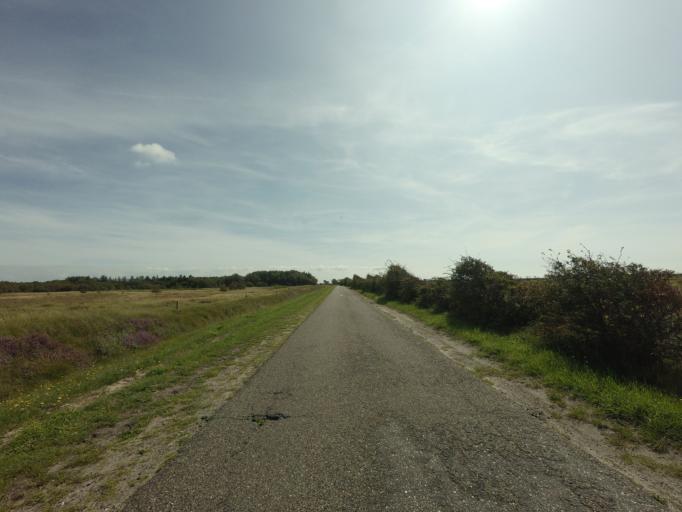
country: NL
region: Friesland
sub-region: Gemeente Ameland
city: Hollum
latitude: 53.4449
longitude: 5.6621
